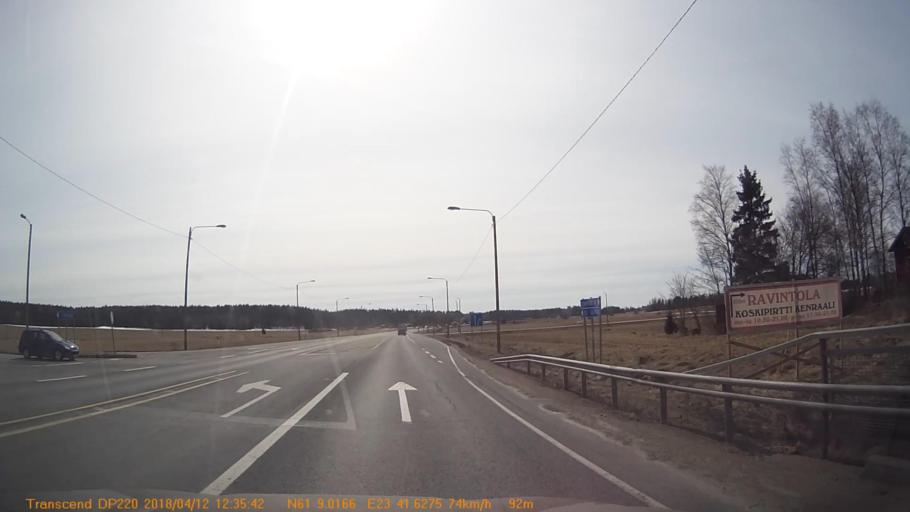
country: FI
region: Pirkanmaa
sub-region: Etelae-Pirkanmaa
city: Kylmaekoski
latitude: 61.1505
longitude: 23.6939
